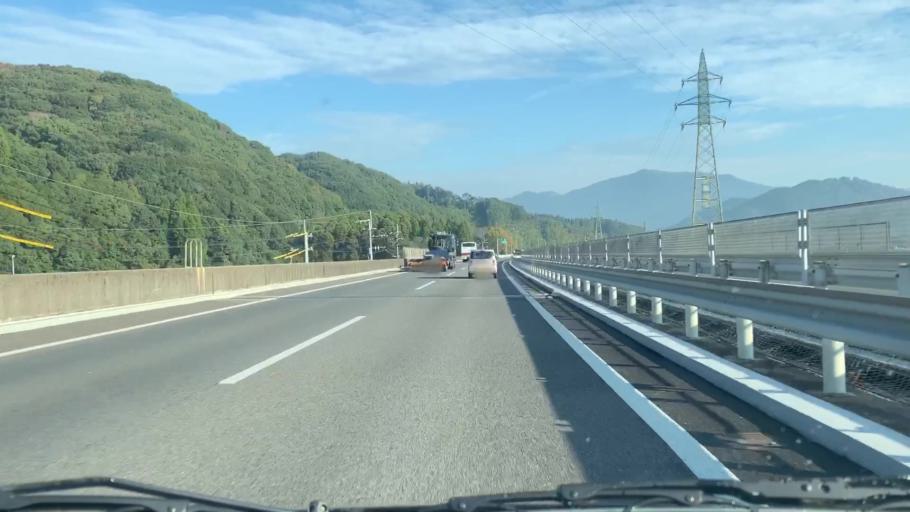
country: JP
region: Saga Prefecture
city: Takeocho-takeo
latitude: 33.2579
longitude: 130.0806
